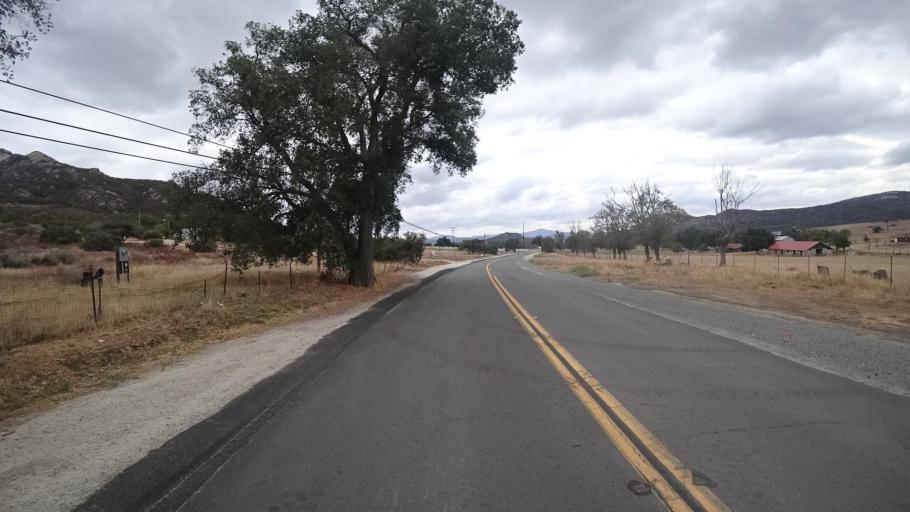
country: US
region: California
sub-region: San Diego County
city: Campo
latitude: 32.6551
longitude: -116.4967
